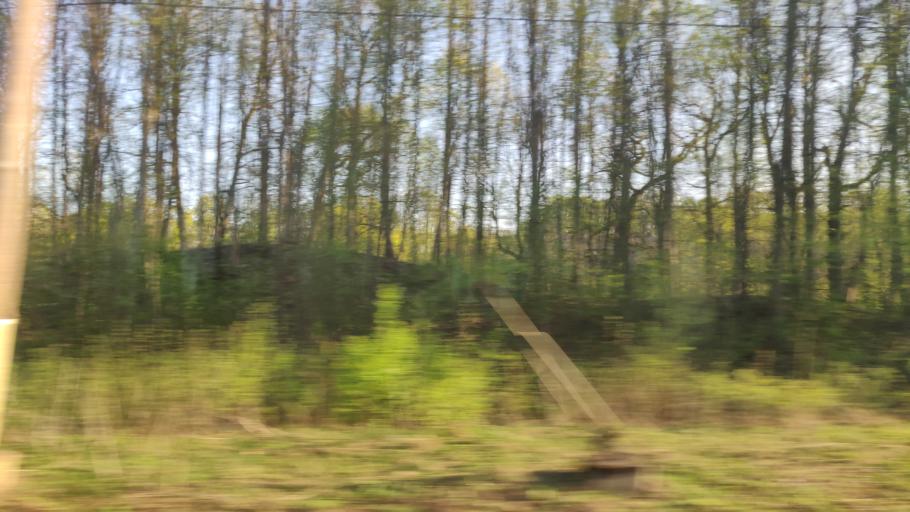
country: LT
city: Grigiskes
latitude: 54.6330
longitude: 25.1074
